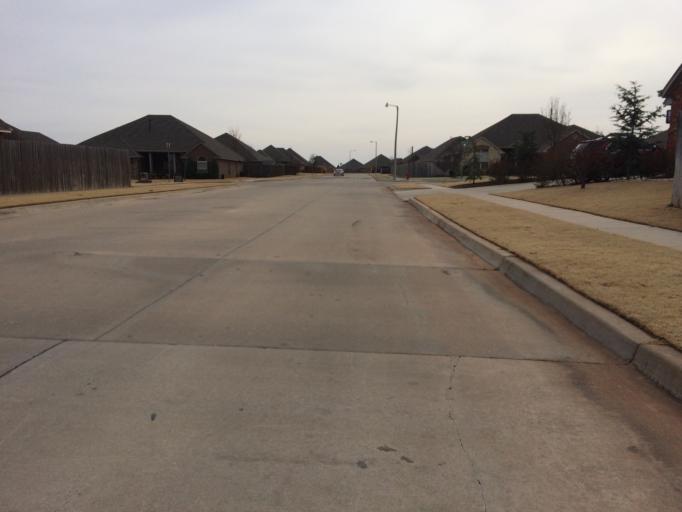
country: US
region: Oklahoma
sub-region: Cleveland County
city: Hall Park
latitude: 35.2147
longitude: -97.3942
